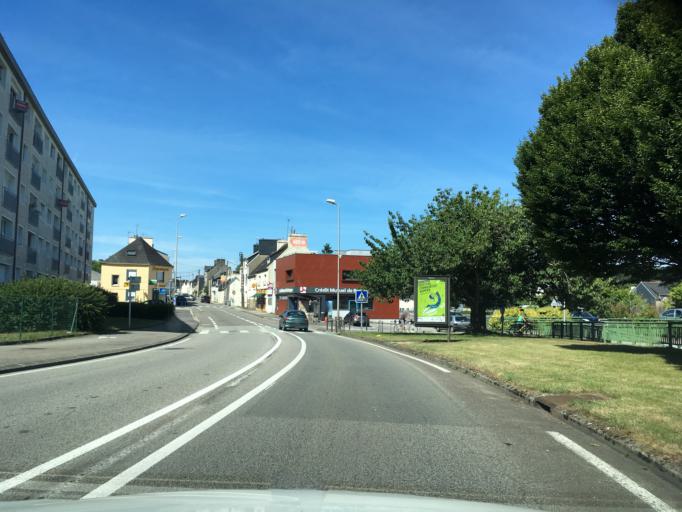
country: FR
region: Brittany
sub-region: Departement du Finistere
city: Quimper
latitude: 47.9802
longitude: -4.1217
